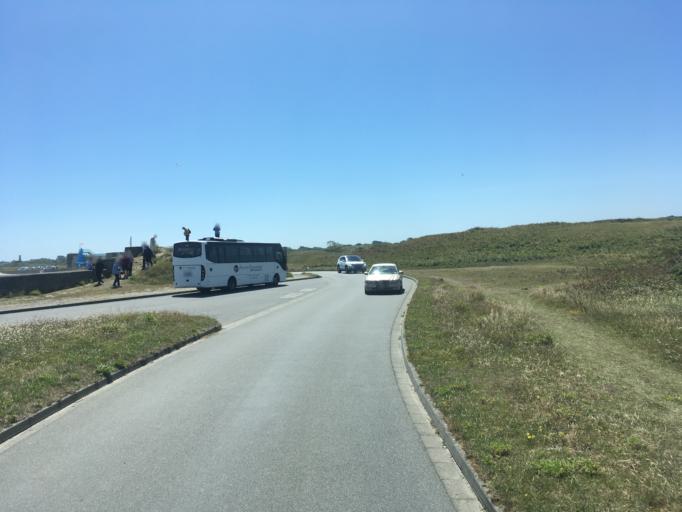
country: GG
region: St Peter Port
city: Saint Peter Port
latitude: 49.5047
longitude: -2.5344
